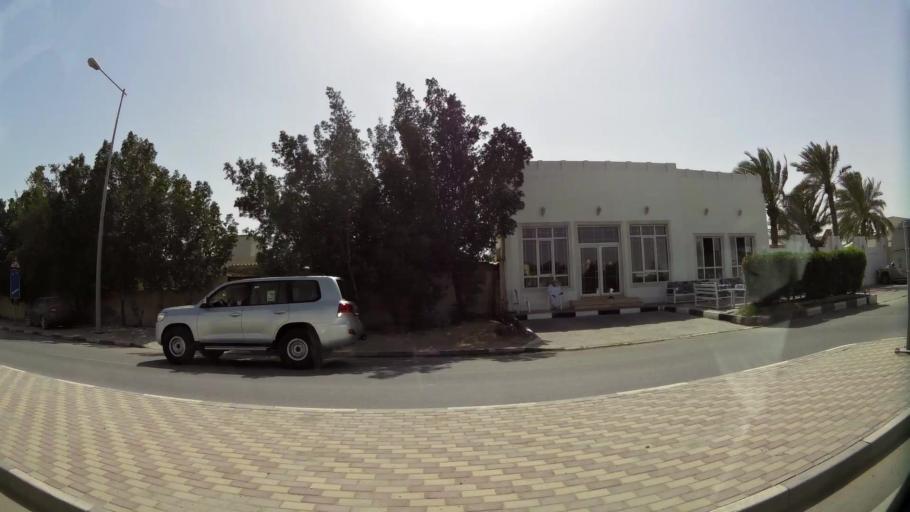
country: QA
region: Baladiyat Umm Salal
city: Umm Salal Muhammad
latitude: 25.3994
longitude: 51.4234
